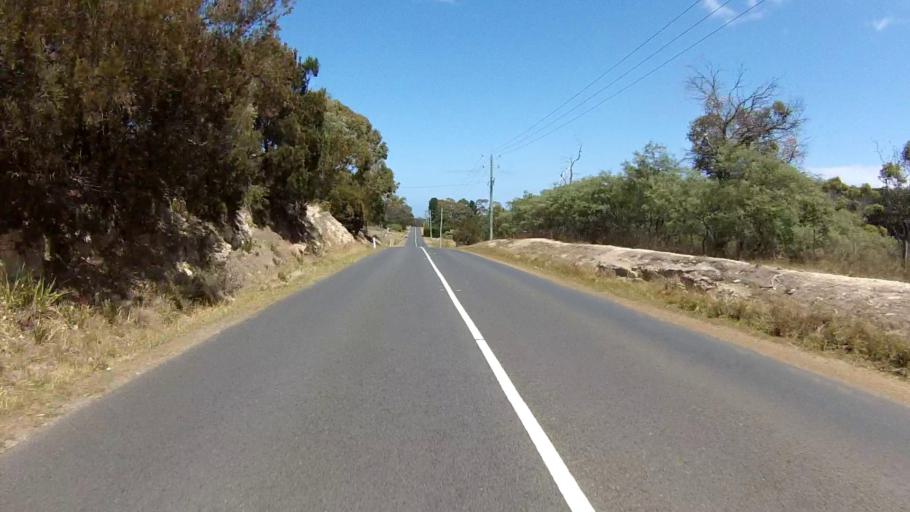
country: AU
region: Tasmania
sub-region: Clarence
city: Sandford
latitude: -42.9583
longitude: 147.4750
